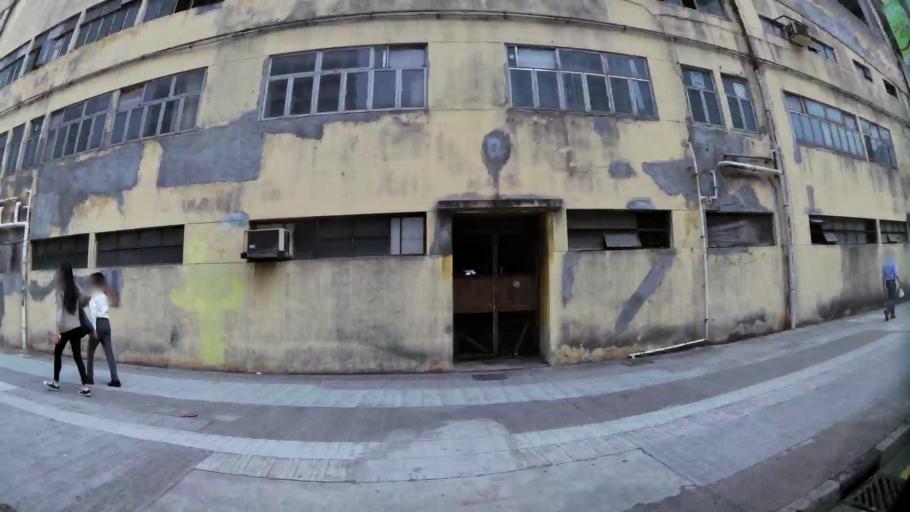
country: HK
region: Wanchai
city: Wan Chai
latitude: 22.2659
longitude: 114.2449
